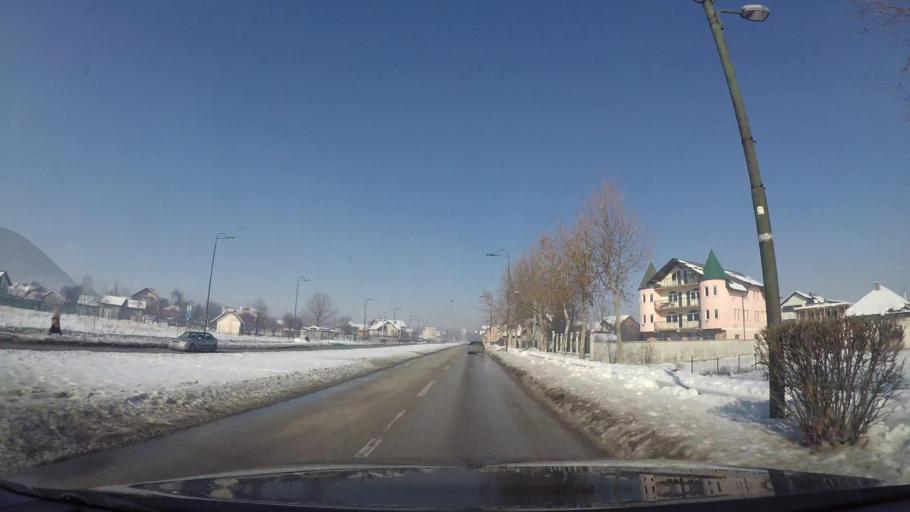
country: BA
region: Federation of Bosnia and Herzegovina
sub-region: Kanton Sarajevo
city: Sarajevo
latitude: 43.8141
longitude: 18.3092
